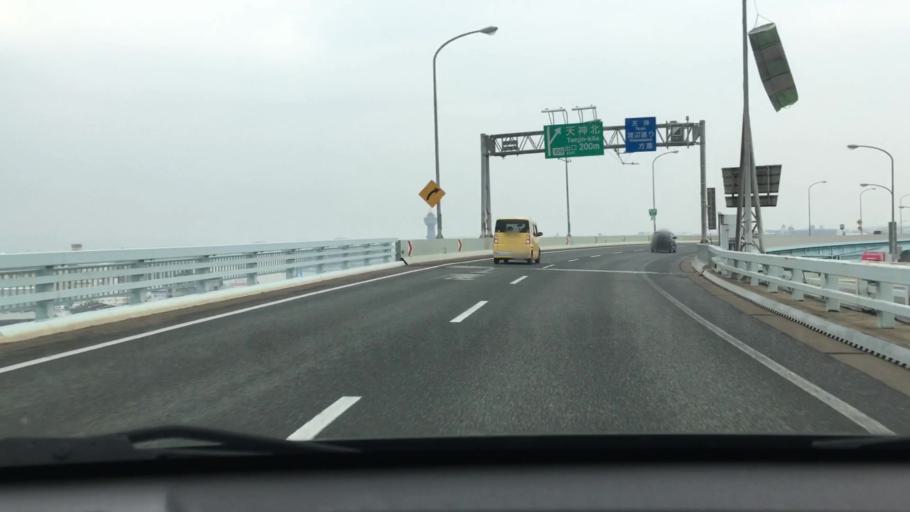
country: JP
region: Fukuoka
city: Fukuoka-shi
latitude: 33.6002
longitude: 130.3848
